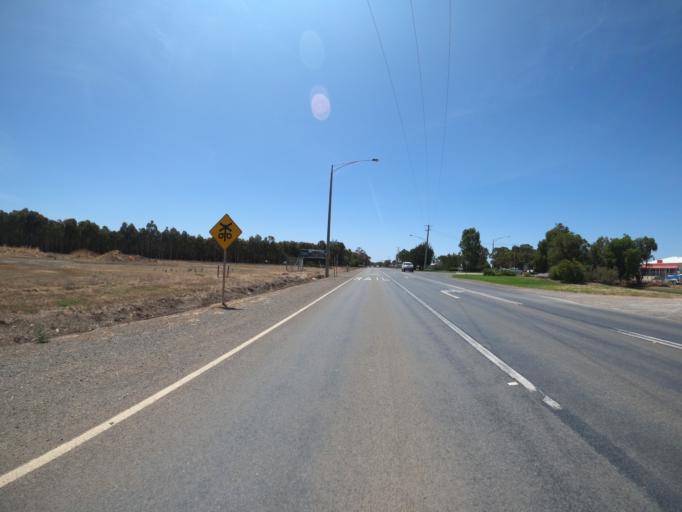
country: AU
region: Victoria
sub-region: Moira
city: Yarrawonga
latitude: -36.0274
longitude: 145.9955
